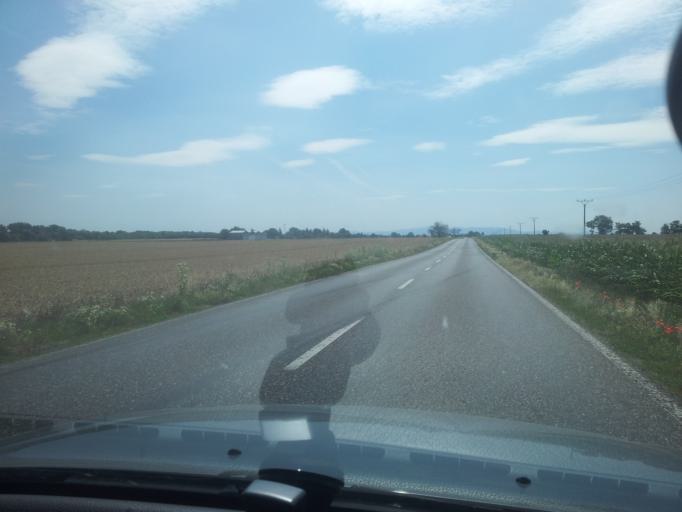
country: SK
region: Nitriansky
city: Levice
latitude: 48.1735
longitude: 18.5356
